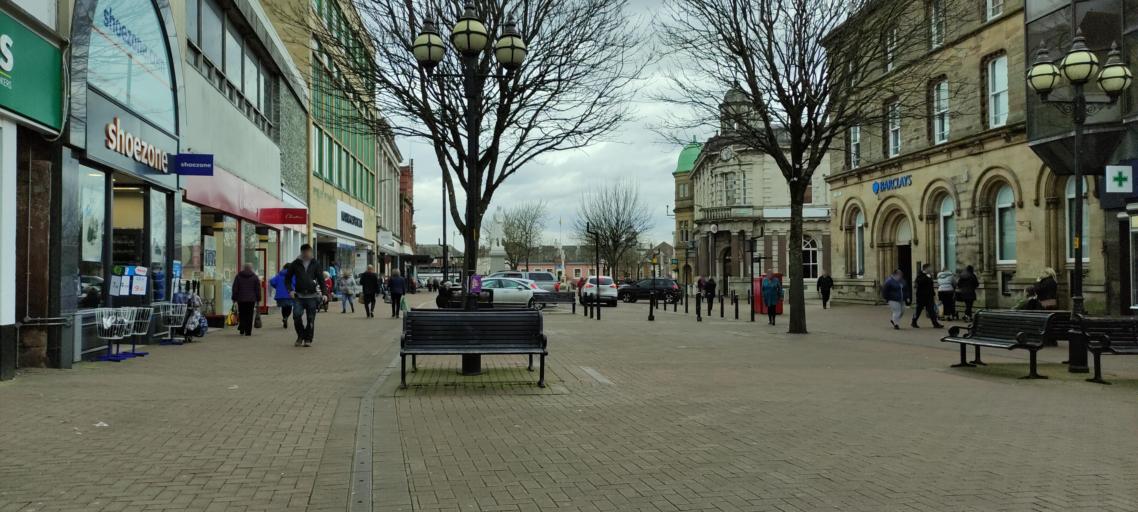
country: GB
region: England
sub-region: Cumbria
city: Carlisle
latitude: 54.8933
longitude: -2.9350
